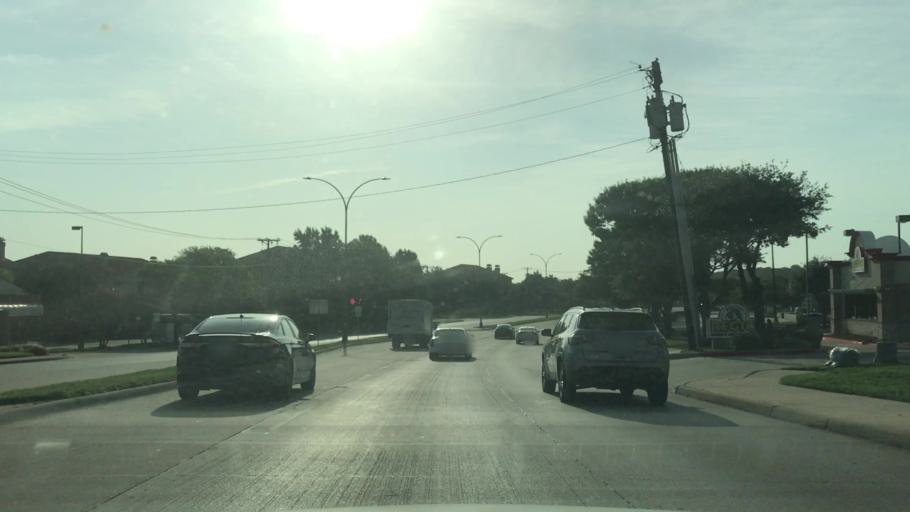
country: US
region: Texas
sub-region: Tarrant County
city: Arlington
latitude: 32.7845
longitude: -97.0946
